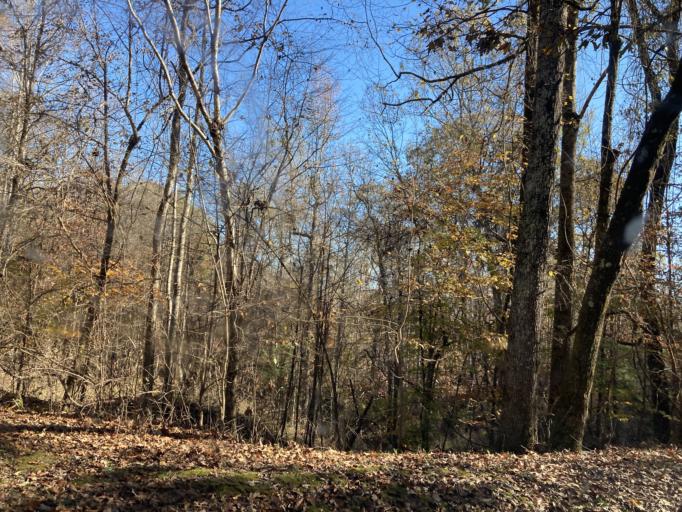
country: US
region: Mississippi
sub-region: Madison County
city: Kearney Park
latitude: 32.6673
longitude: -90.5096
